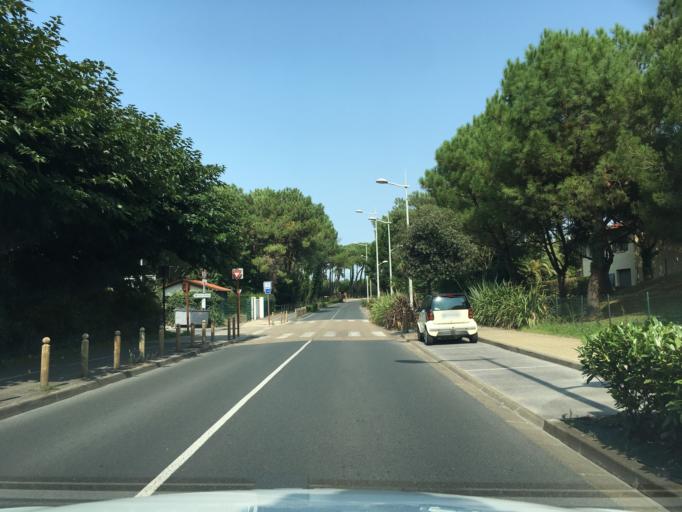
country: FR
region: Aquitaine
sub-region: Departement des Pyrenees-Atlantiques
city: Biarritz
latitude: 43.5066
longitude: -1.5339
